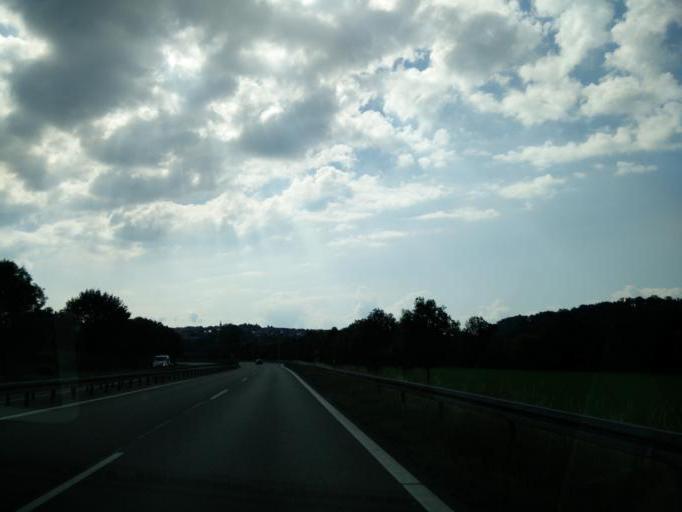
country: DE
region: Baden-Wuerttemberg
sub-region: Tuebingen Region
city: Kusterdingen
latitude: 48.5363
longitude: 9.1289
